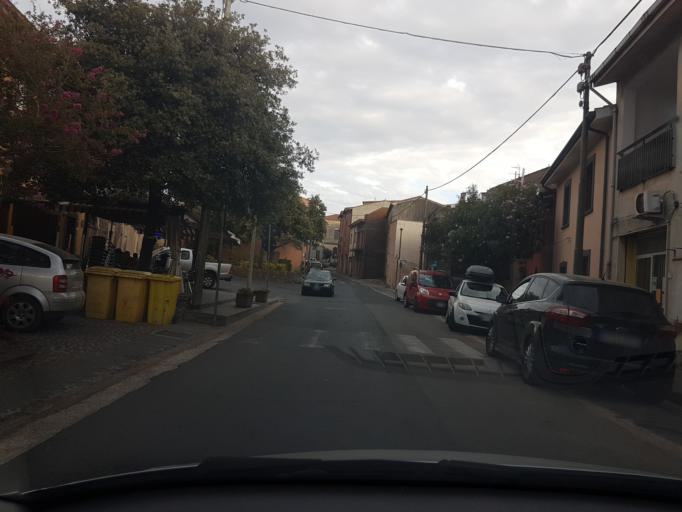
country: IT
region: Sardinia
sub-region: Provincia di Oristano
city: Seneghe
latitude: 40.0814
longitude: 8.6104
